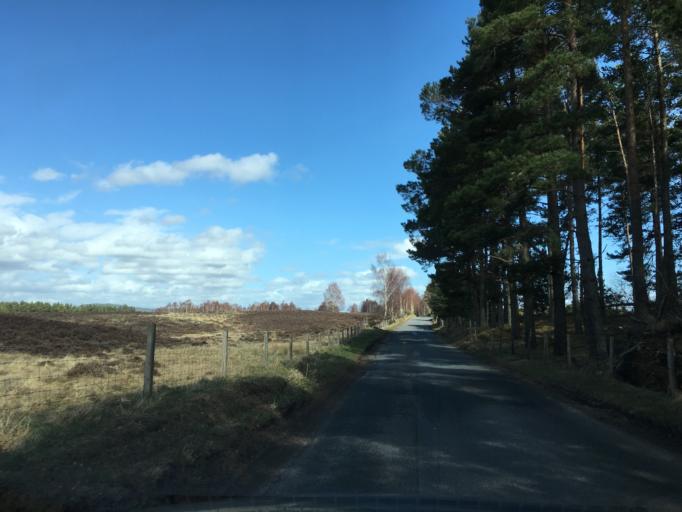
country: GB
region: Scotland
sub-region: Highland
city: Aviemore
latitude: 57.2011
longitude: -3.7979
